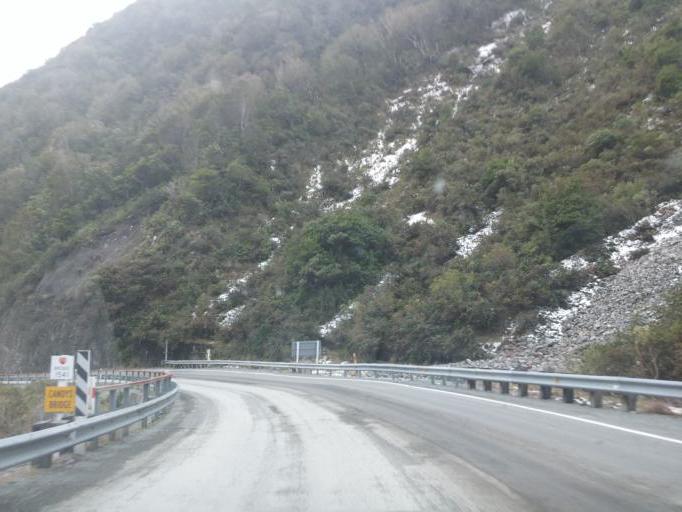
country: NZ
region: West Coast
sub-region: Grey District
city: Greymouth
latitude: -42.8809
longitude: 171.5568
